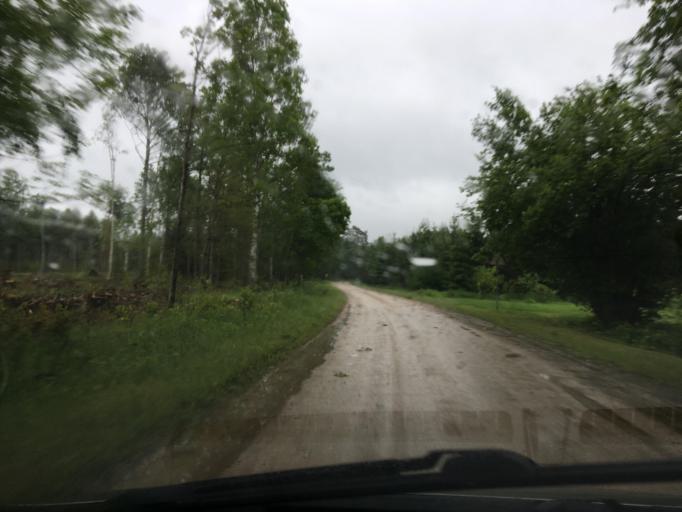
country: EE
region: Laeaene
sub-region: Lihula vald
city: Lihula
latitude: 58.6304
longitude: 23.8109
